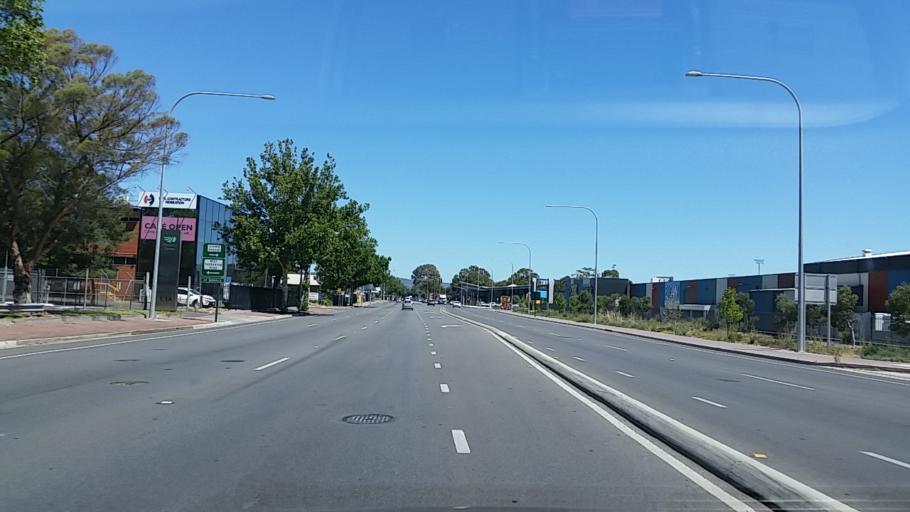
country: AU
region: South Australia
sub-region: City of West Torrens
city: Thebarton
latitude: -34.9125
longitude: 138.5647
